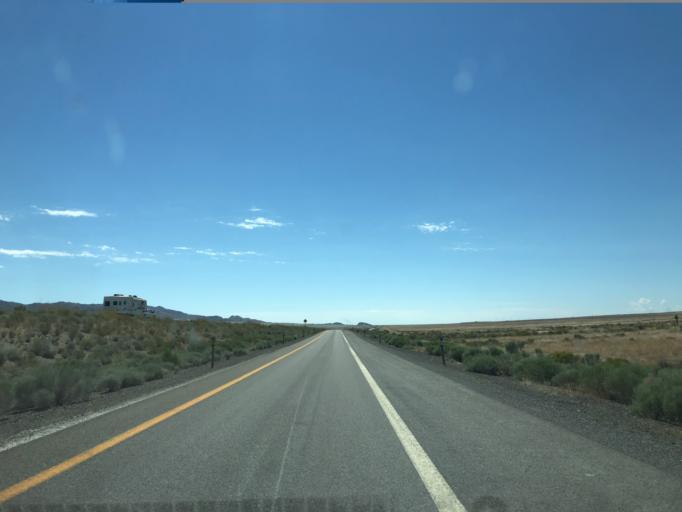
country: US
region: Nevada
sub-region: Elko County
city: West Wendover
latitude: 40.8417
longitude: -114.2097
